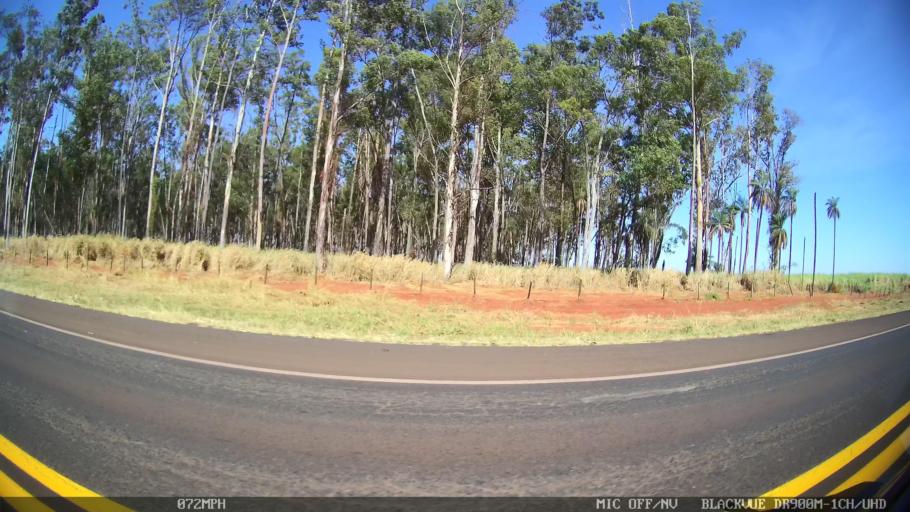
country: BR
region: Sao Paulo
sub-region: Barretos
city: Barretos
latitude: -20.4939
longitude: -48.5282
